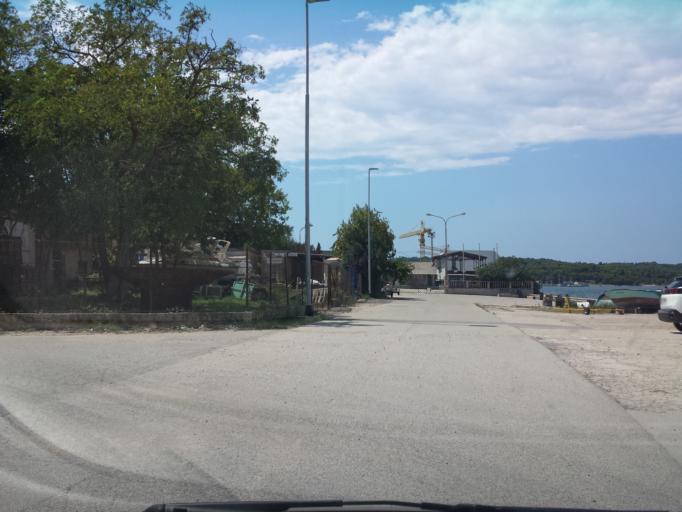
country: HR
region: Istarska
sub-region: Grad Pula
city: Pula
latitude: 44.8638
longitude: 13.8263
